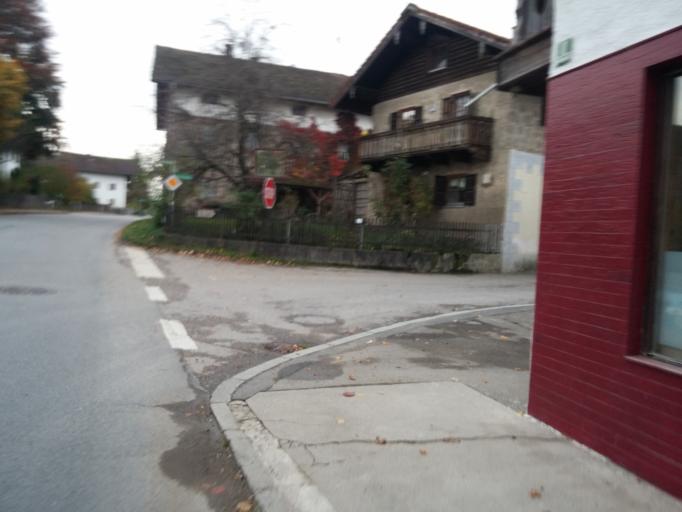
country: DE
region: Bavaria
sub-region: Upper Bavaria
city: Assling
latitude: 48.0230
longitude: 11.9930
